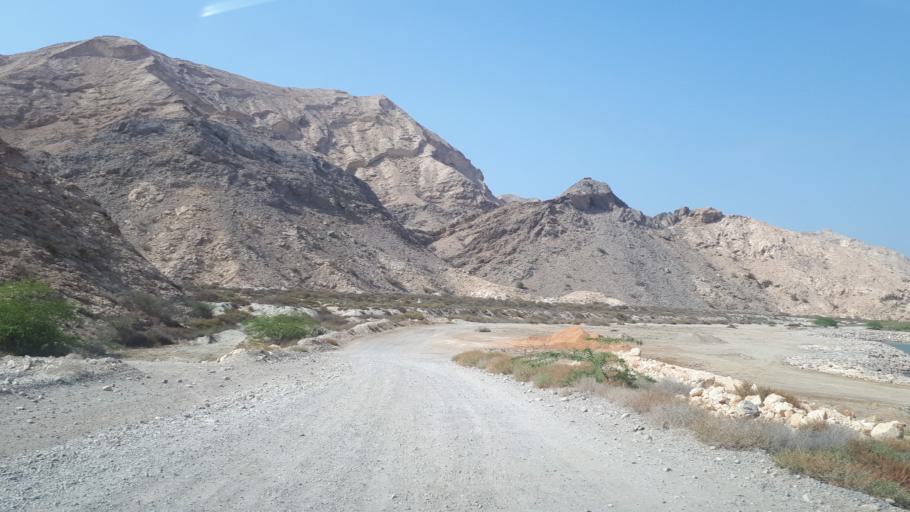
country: OM
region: Muhafazat Masqat
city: Muscat
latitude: 23.5361
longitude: 58.6515
